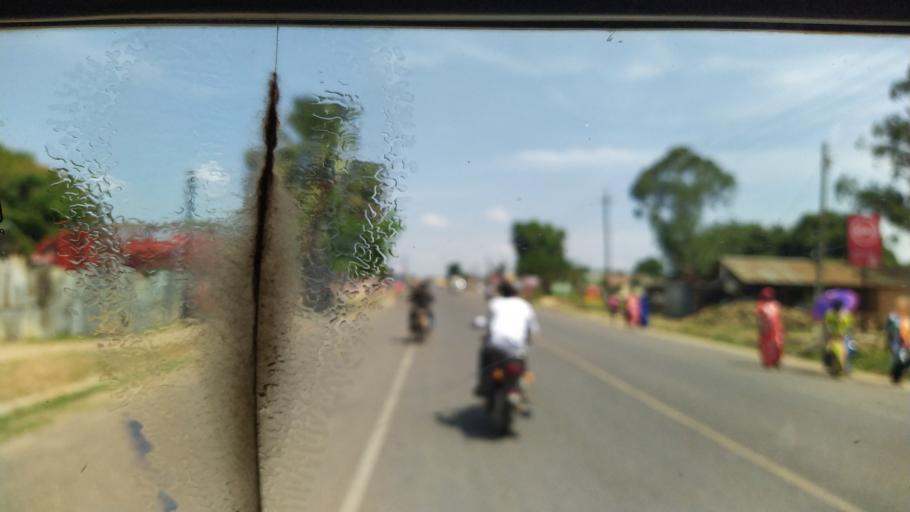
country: UG
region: Northern Region
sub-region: Arua District
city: Arua
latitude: 3.0353
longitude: 30.9133
